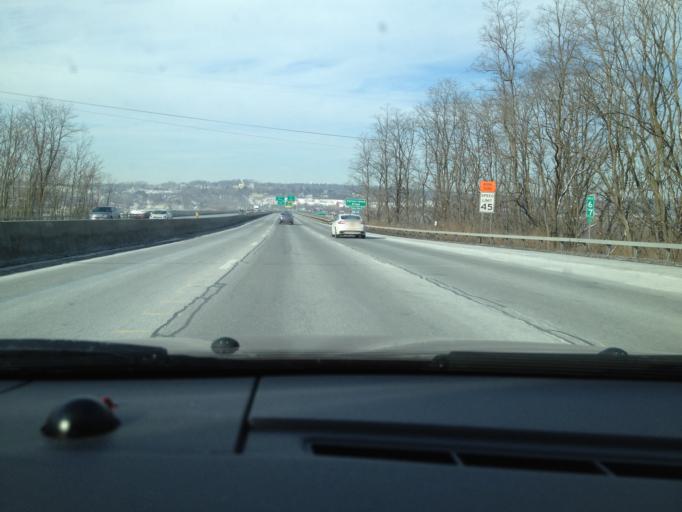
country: US
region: New York
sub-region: Rensselaer County
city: Rensselaer
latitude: 42.6626
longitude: -73.7245
